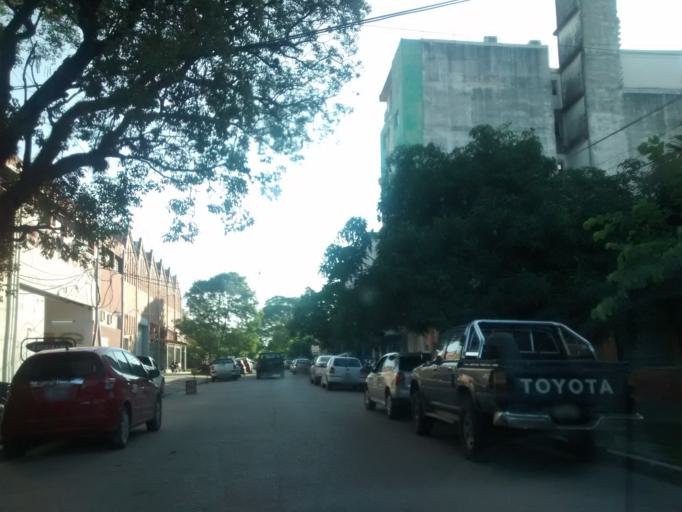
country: AR
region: Chaco
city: Resistencia
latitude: -27.4576
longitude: -58.9815
